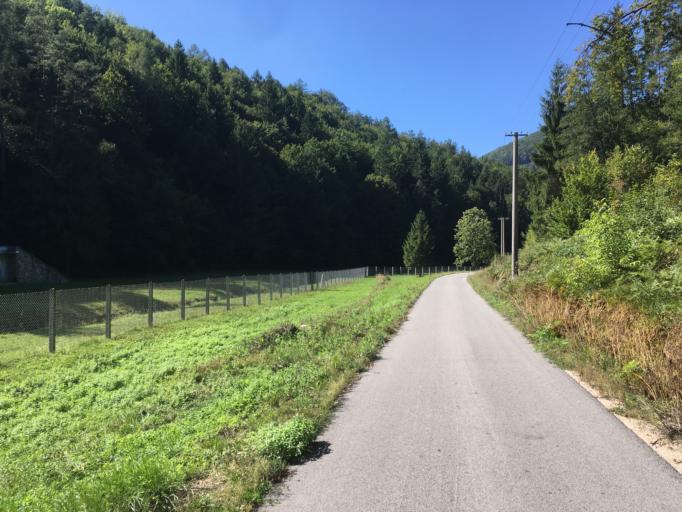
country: SK
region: Trenciansky
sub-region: Okres Povazska Bystrica
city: Povazska Bystrica
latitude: 49.0121
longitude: 18.4460
